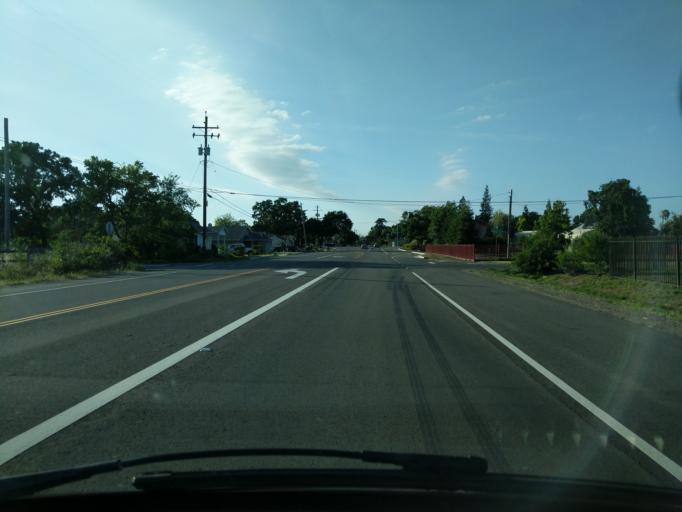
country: US
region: California
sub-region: San Joaquin County
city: Garden Acres
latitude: 37.9495
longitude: -121.2424
